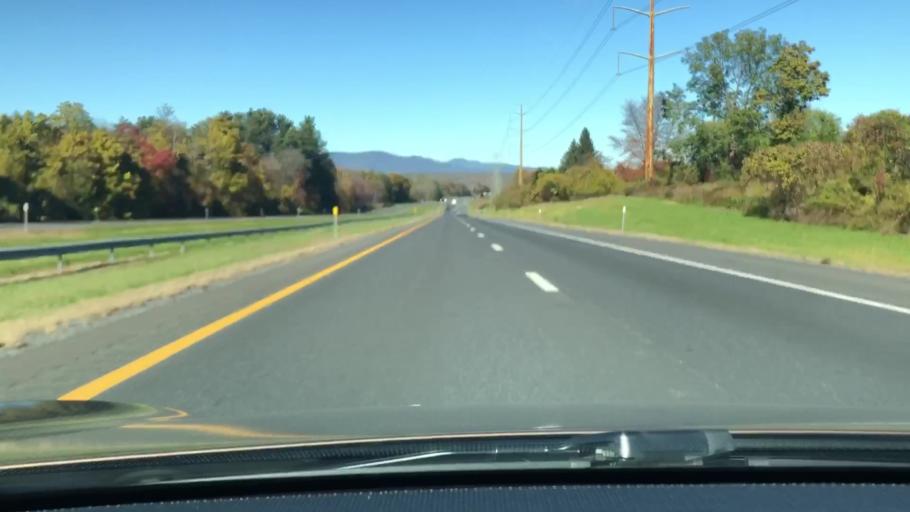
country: US
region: New York
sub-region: Ulster County
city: Hurley
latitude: 41.9113
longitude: -74.0431
